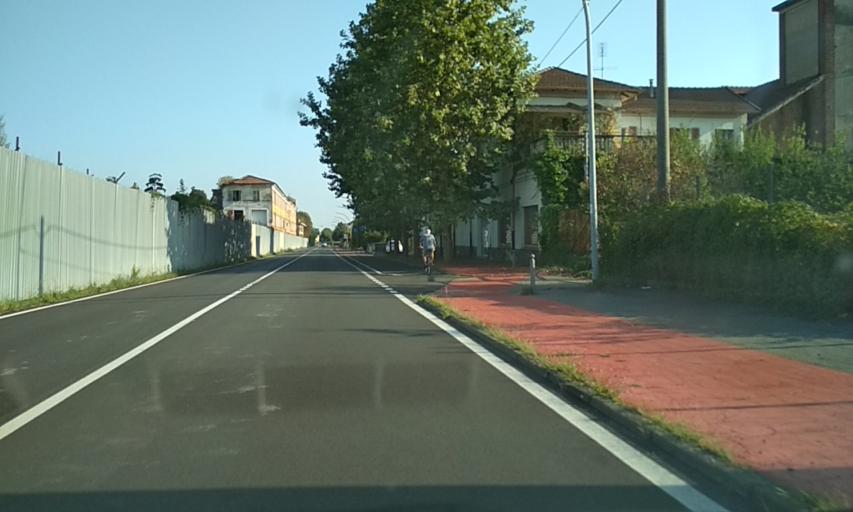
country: IT
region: Piedmont
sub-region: Provincia di Torino
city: Rivarolo Canavese
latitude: 45.3243
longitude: 7.7278
